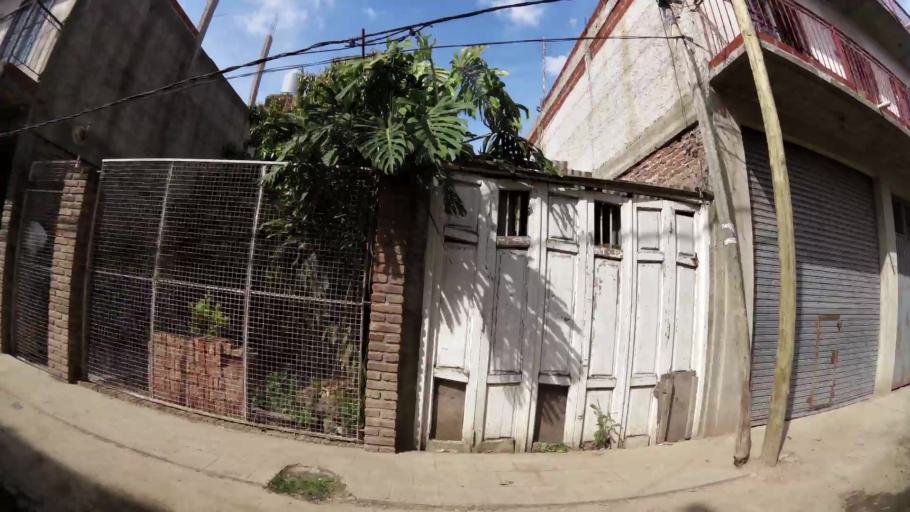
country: AR
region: Buenos Aires
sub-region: Partido de Quilmes
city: Quilmes
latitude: -34.7636
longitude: -58.2490
